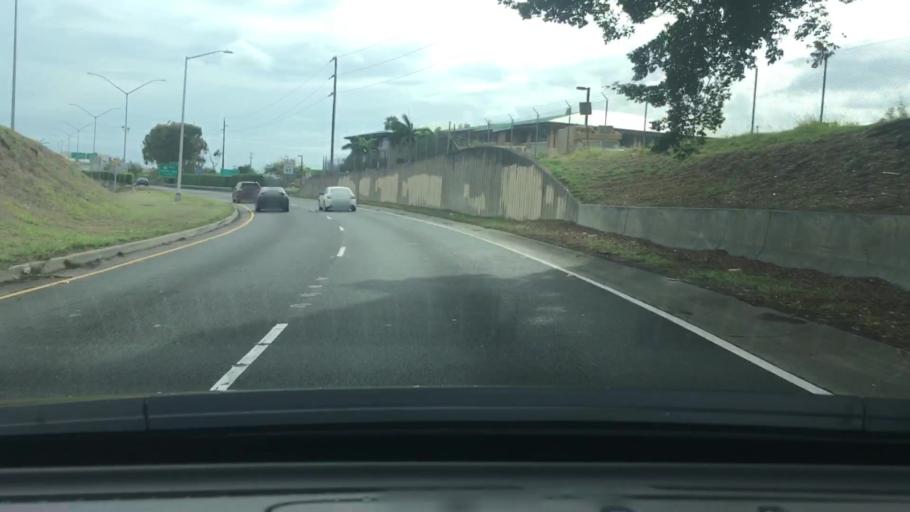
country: US
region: Hawaii
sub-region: Honolulu County
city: Honolulu
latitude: 21.3378
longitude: -157.8846
